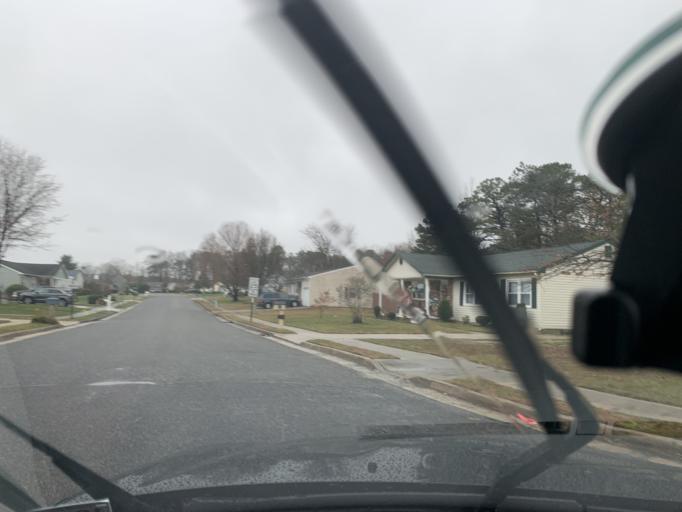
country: US
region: New Jersey
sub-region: Atlantic County
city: Pomona
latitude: 39.4353
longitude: -74.5932
